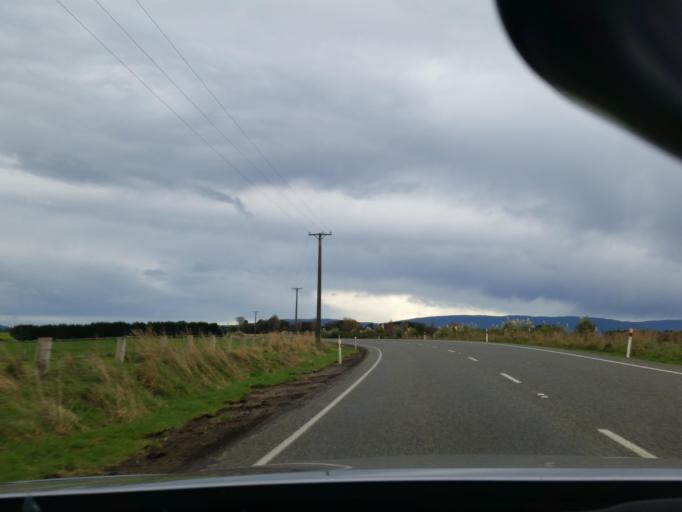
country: NZ
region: Southland
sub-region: Southland District
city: Riverton
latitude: -46.2954
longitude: 168.1295
